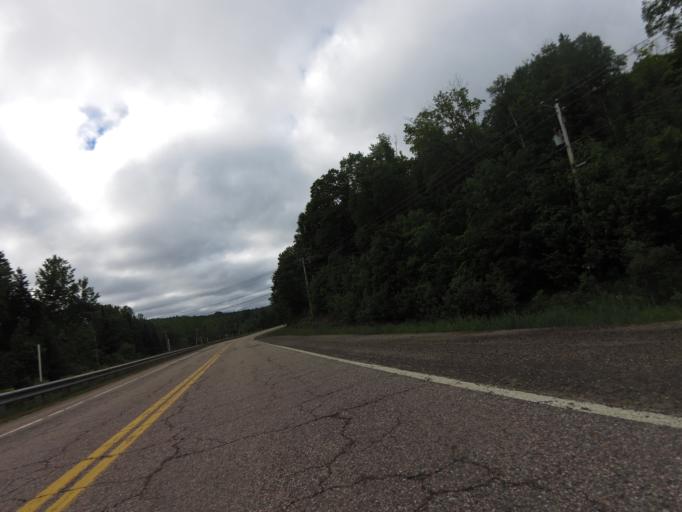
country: CA
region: Quebec
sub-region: Outaouais
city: Shawville
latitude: 45.8309
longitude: -76.4614
